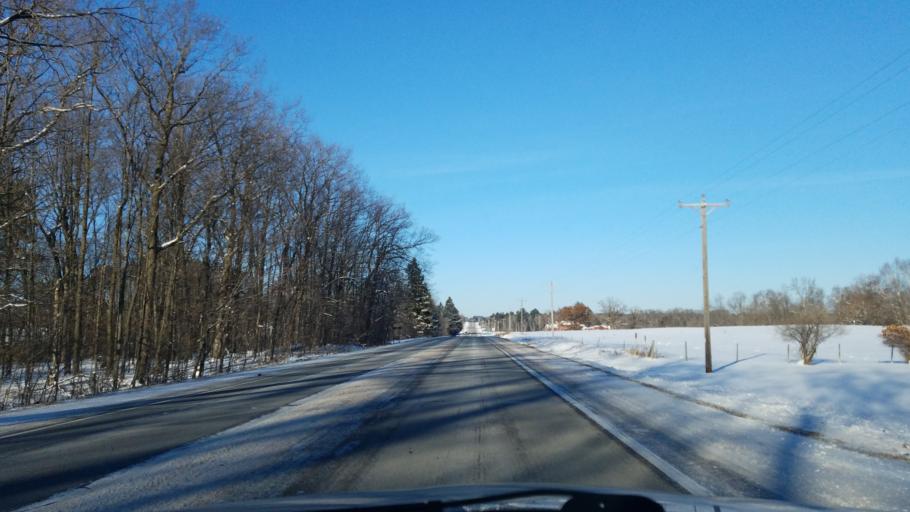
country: US
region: Wisconsin
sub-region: Barron County
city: Cumberland
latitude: 45.5035
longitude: -92.0524
